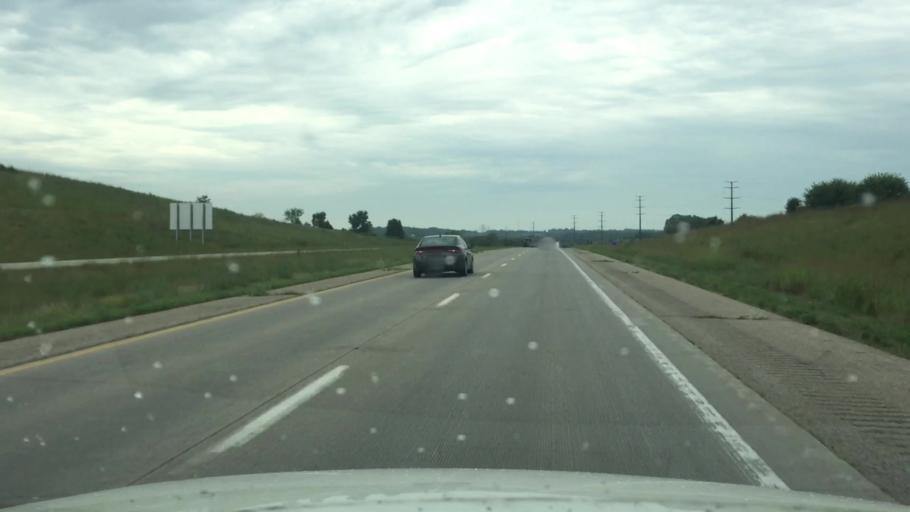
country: US
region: Iowa
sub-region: Warren County
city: Norwalk
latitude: 41.5006
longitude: -93.5994
